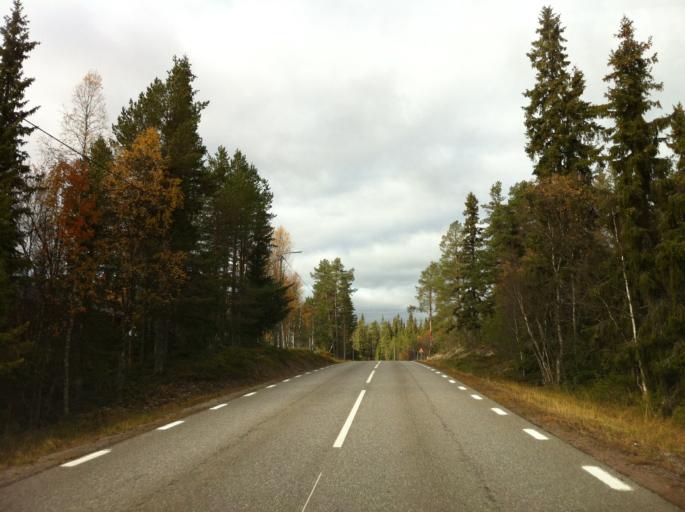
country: NO
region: Hedmark
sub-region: Engerdal
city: Engerdal
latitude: 62.0010
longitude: 12.4465
